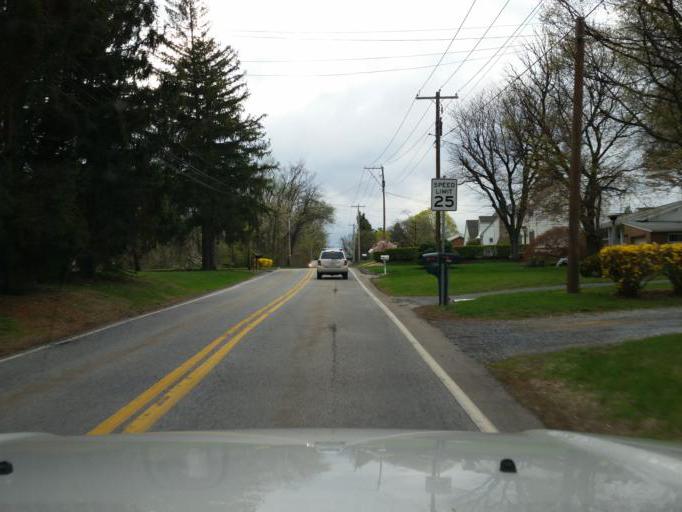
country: US
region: Pennsylvania
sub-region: Dauphin County
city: Paxtonia
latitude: 40.3053
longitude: -76.7909
